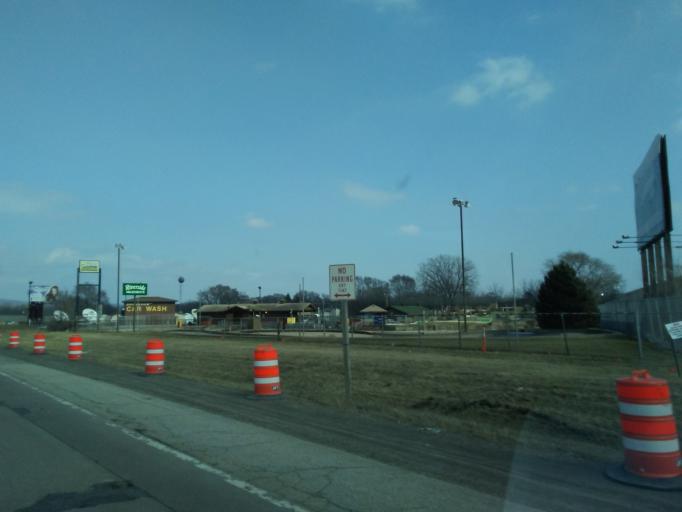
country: US
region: Wisconsin
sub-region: La Crosse County
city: North La Crosse
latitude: 43.8608
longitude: -91.2404
